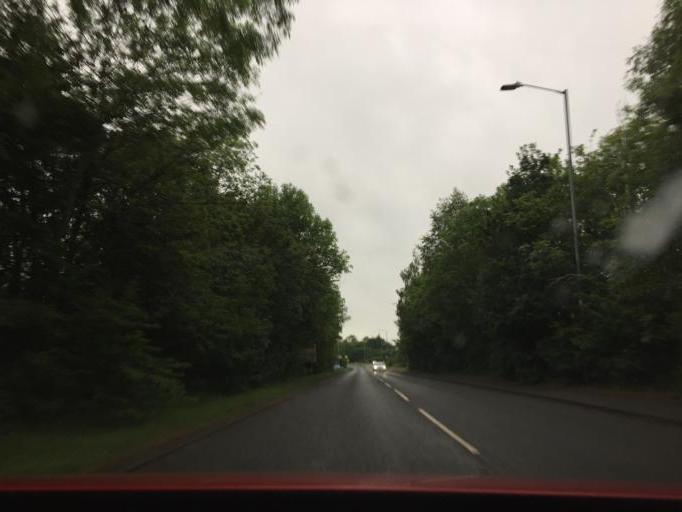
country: GB
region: England
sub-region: Warwickshire
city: Attleborough
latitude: 52.5202
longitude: -1.4411
